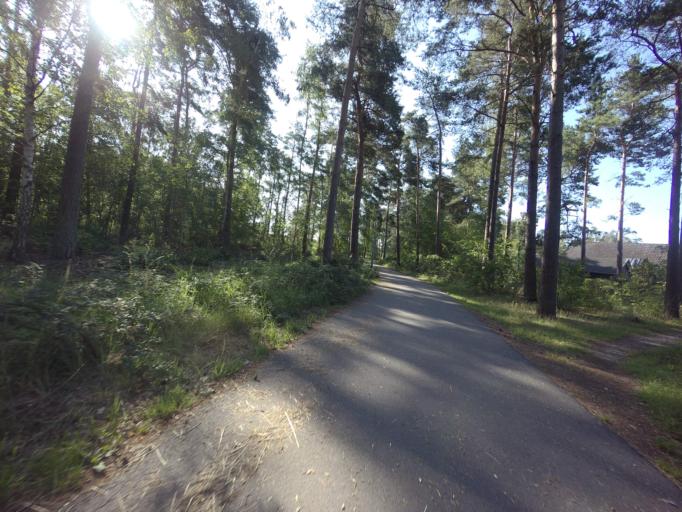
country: SE
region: Skane
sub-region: Kavlinge Kommun
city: Hofterup
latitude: 55.8039
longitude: 12.9770
